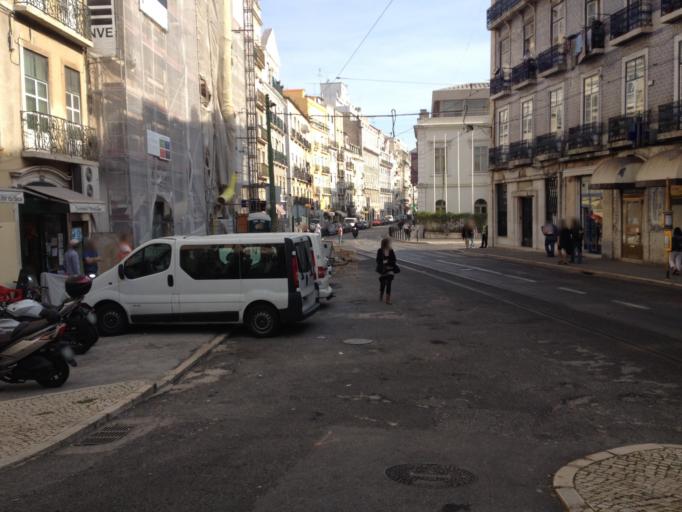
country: PT
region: Lisbon
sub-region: Lisbon
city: Lisbon
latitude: 38.7085
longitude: -9.1474
